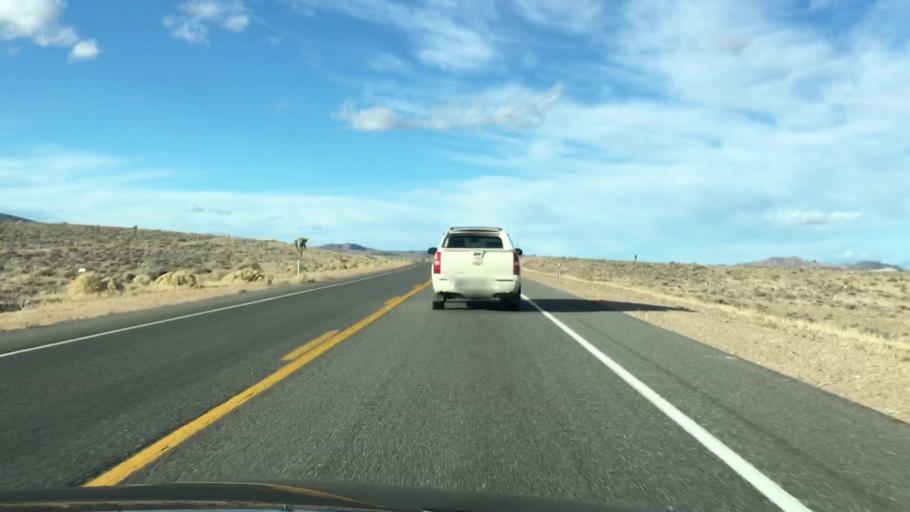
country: US
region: Nevada
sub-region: Esmeralda County
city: Goldfield
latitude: 37.5652
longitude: -117.1997
